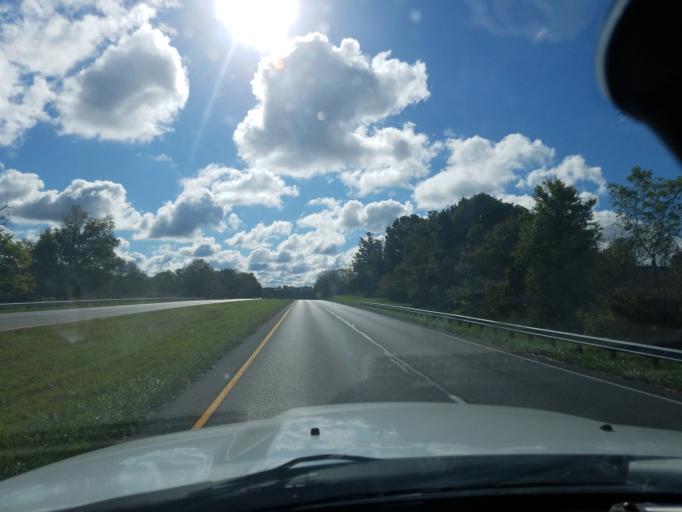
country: US
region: Kentucky
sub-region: Lincoln County
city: Stanford
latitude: 37.5788
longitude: -84.7064
